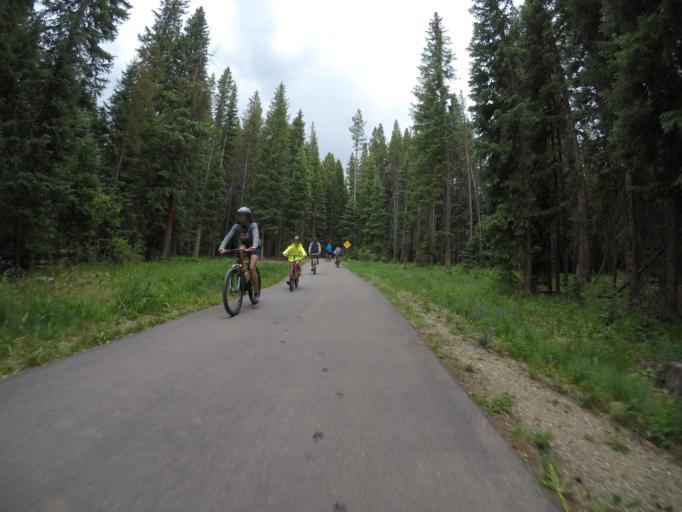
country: US
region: Colorado
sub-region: Grand County
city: Fraser
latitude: 39.9060
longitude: -105.7791
